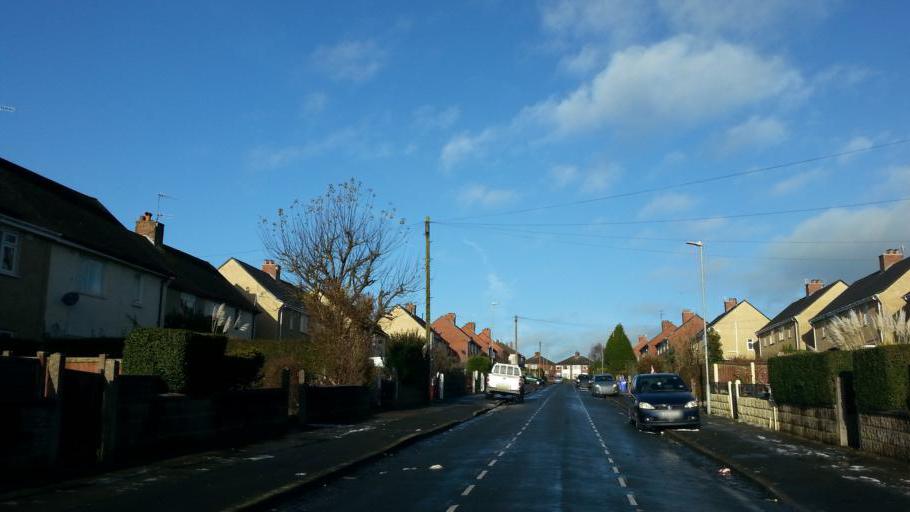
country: GB
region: England
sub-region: Stoke-on-Trent
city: Stoke-on-Trent
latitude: 52.9867
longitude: -2.1638
